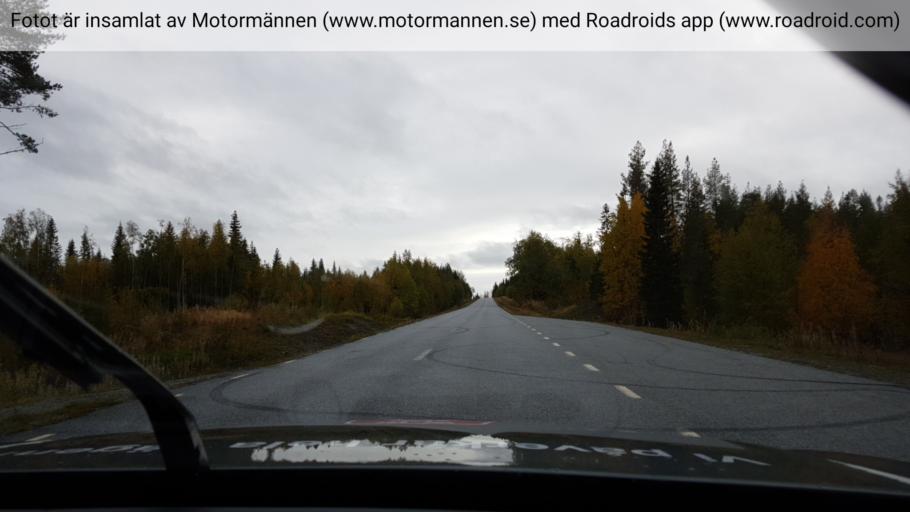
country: SE
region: Vaesterbotten
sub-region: Vilhelmina Kommun
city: Sjoberg
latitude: 64.8171
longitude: 15.9682
